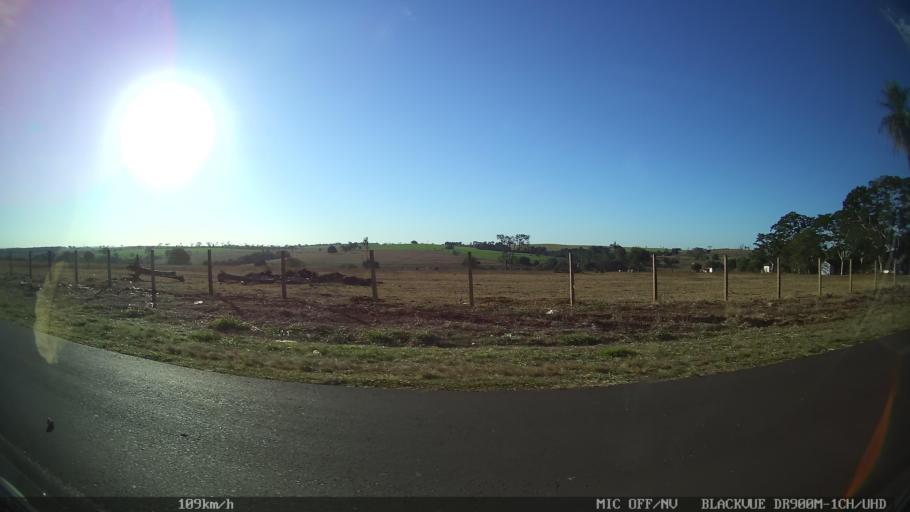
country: BR
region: Sao Paulo
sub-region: Guapiacu
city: Guapiacu
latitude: -20.7890
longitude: -49.2901
